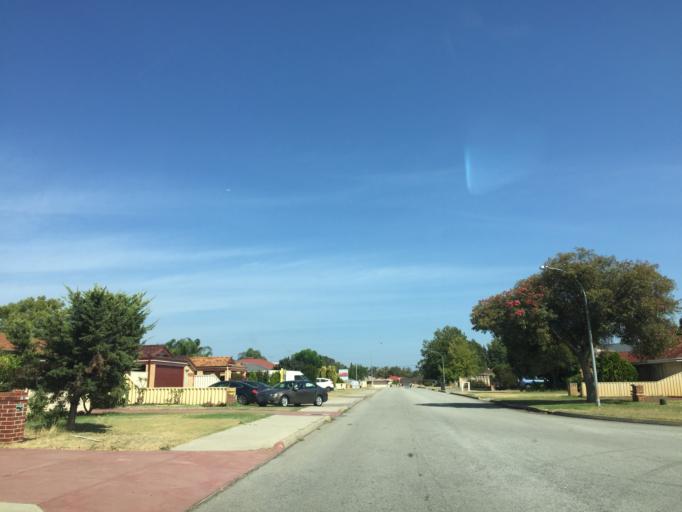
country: AU
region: Western Australia
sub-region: Gosnells
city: Thornlie
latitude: -32.0796
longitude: 115.9589
